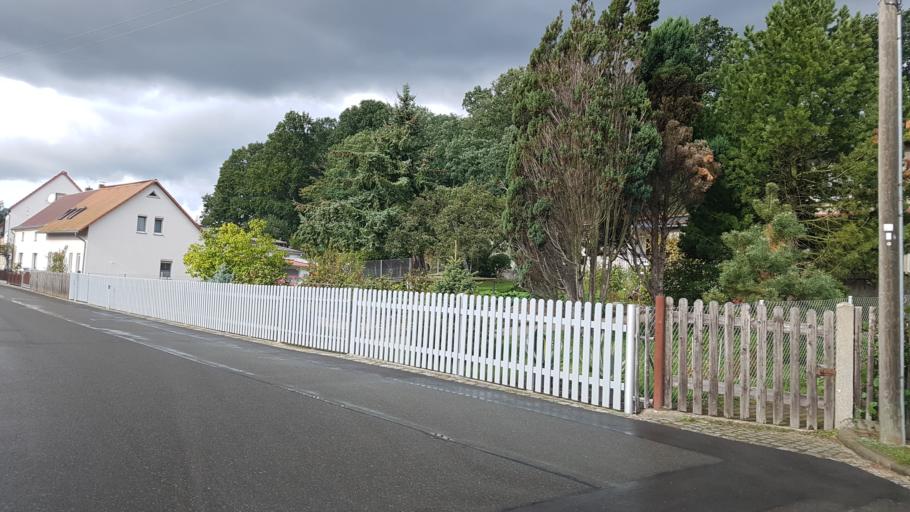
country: DE
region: Saxony
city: Dahlen
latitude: 51.3670
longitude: 13.0072
